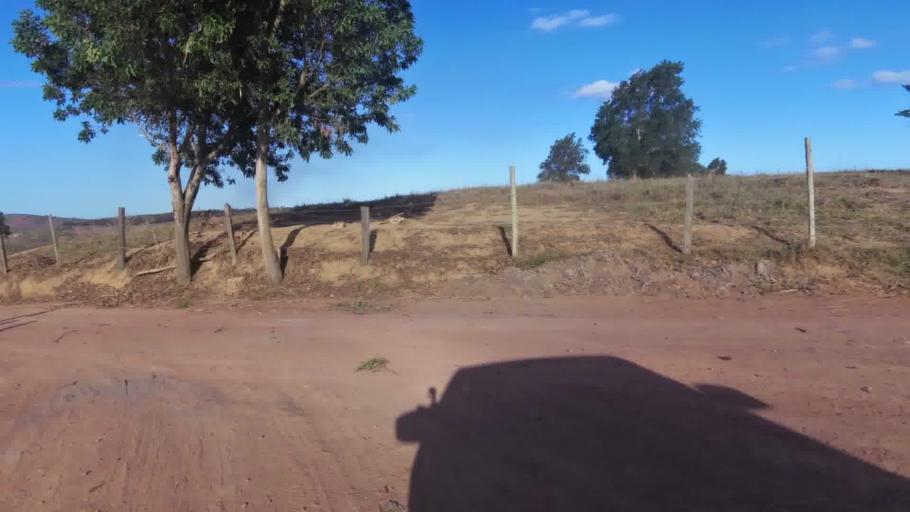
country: BR
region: Espirito Santo
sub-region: Marataizes
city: Marataizes
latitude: -21.1644
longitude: -41.0563
